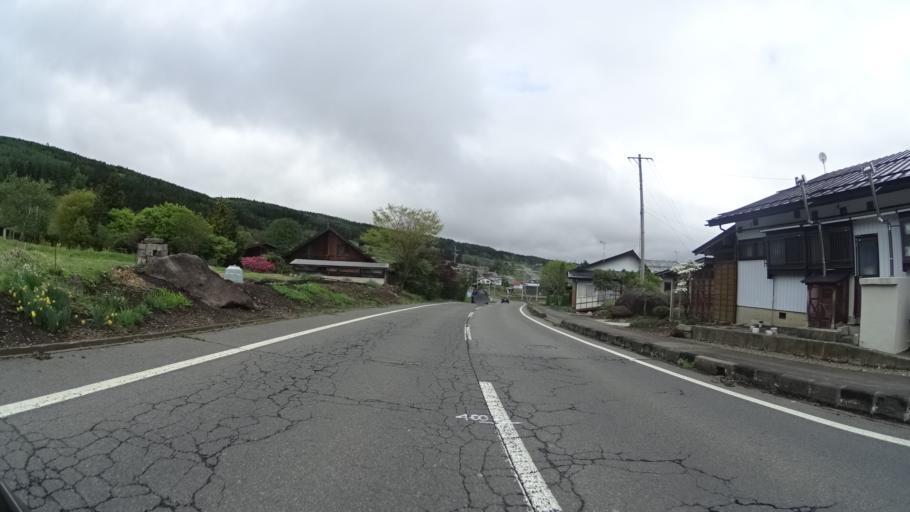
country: JP
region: Nagano
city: Nagano-shi
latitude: 36.7355
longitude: 138.2060
